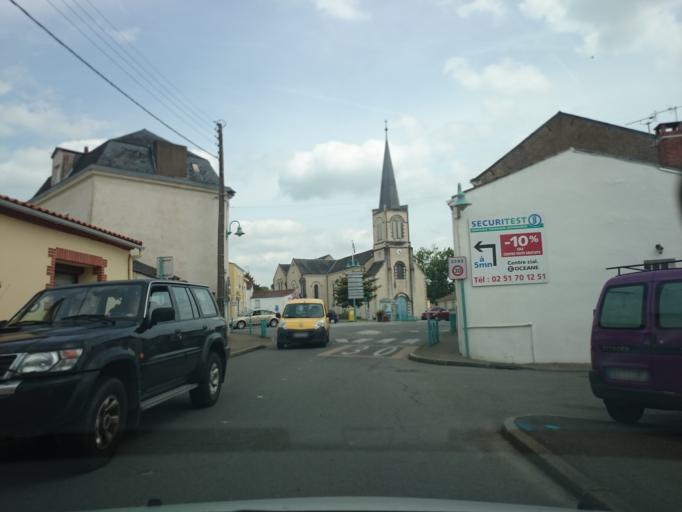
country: FR
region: Pays de la Loire
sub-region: Departement de la Loire-Atlantique
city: Pont-Saint-Martin
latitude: 47.1234
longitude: -1.5848
